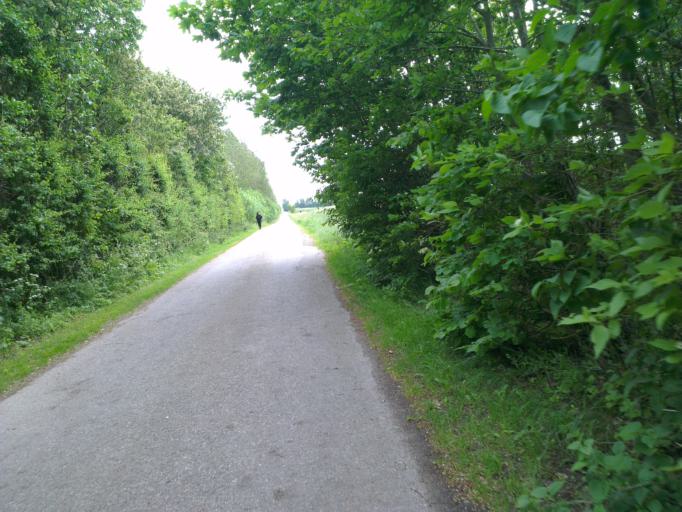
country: DK
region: Capital Region
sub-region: Frederikssund Kommune
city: Frederikssund
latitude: 55.8150
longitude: 12.0771
